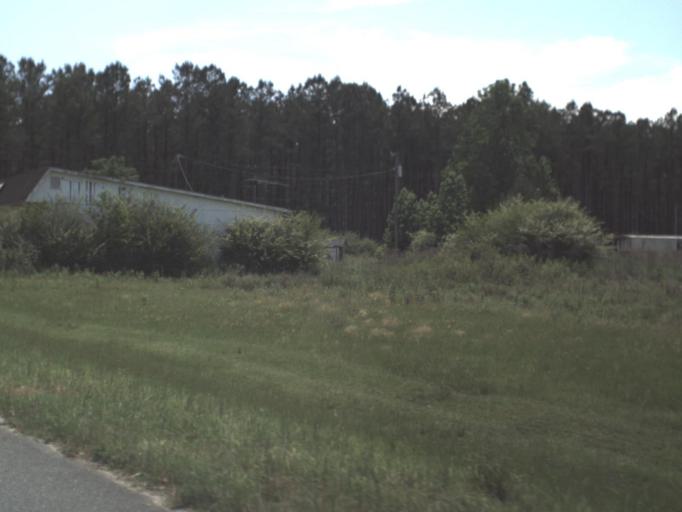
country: US
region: Florida
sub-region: Gulf County
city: Wewahitchka
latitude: 30.2377
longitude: -85.2094
